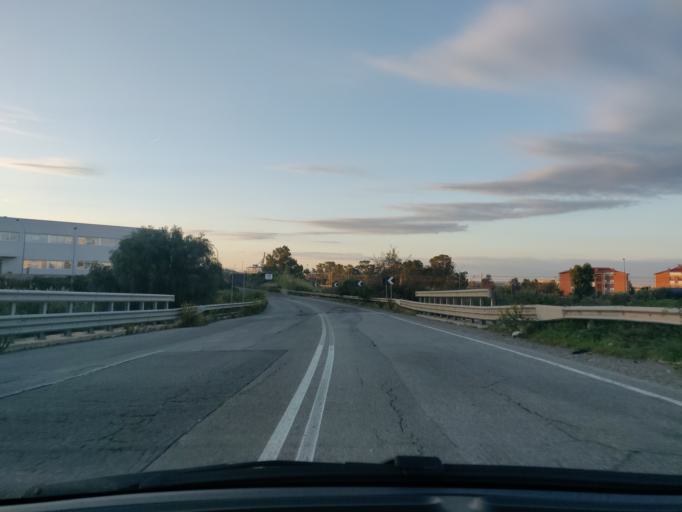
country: IT
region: Latium
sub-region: Citta metropolitana di Roma Capitale
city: Aurelia
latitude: 42.1226
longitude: 11.7704
